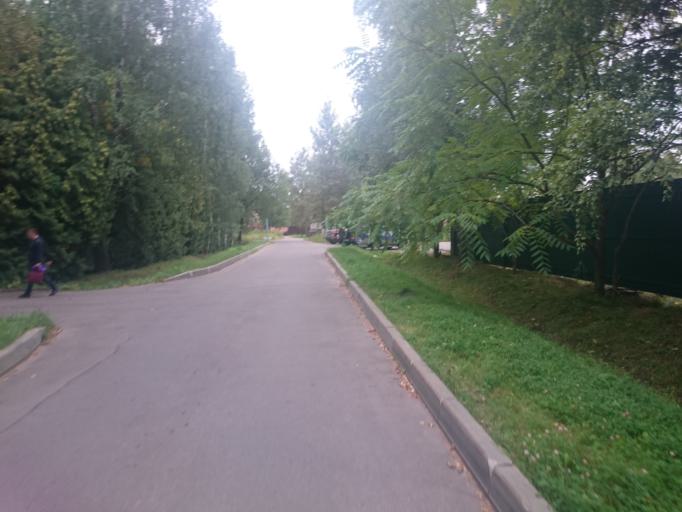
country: RU
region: Moskovskaya
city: Novopodrezkovo
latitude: 55.8955
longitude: 37.3556
